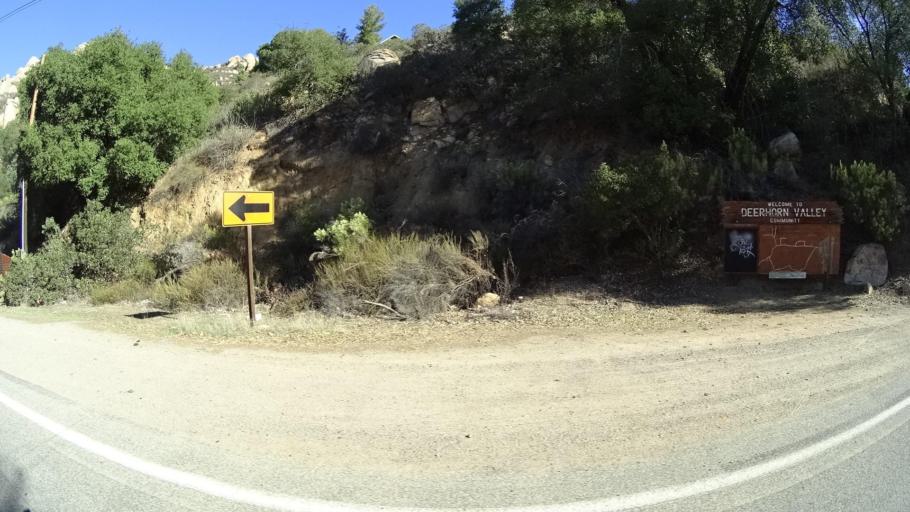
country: US
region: California
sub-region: San Diego County
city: Jamul
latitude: 32.6728
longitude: -116.7655
